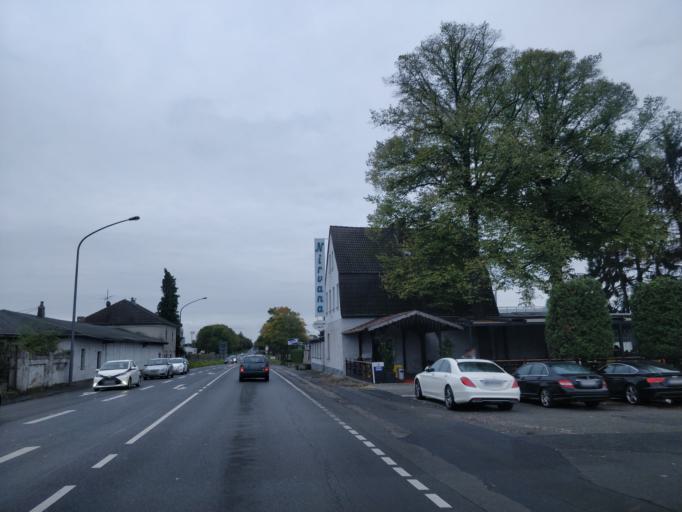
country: DE
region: North Rhine-Westphalia
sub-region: Regierungsbezirk Koln
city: Gremberghoven
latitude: 50.9051
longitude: 7.0631
